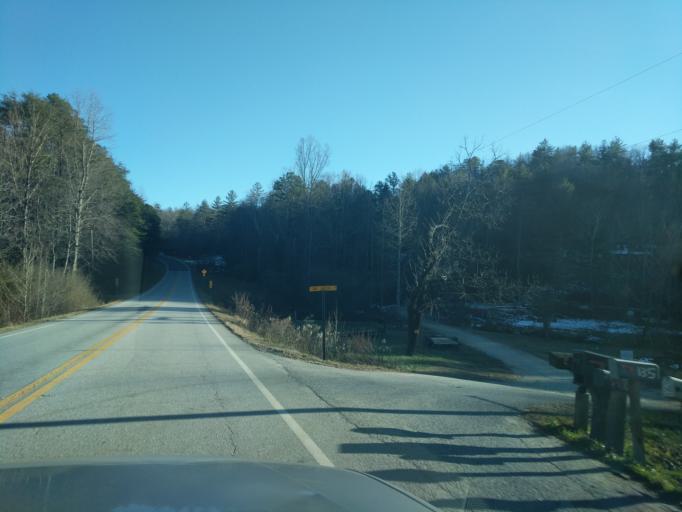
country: US
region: Georgia
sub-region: Rabun County
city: Clayton
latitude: 34.8378
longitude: -83.3325
